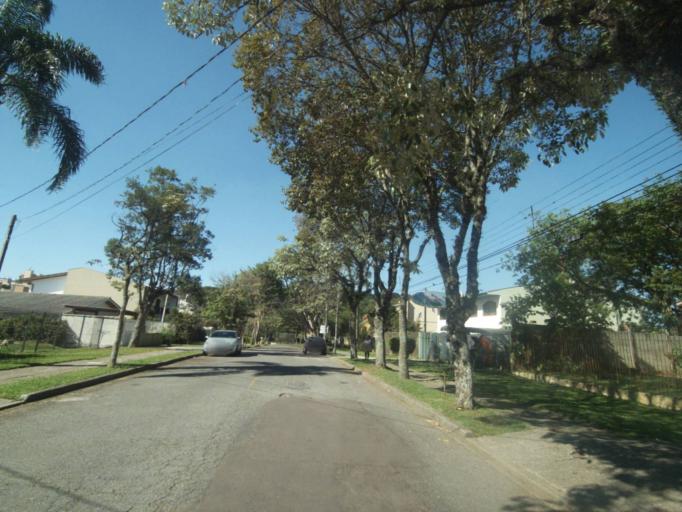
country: BR
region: Parana
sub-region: Curitiba
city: Curitiba
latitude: -25.3901
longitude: -49.2331
